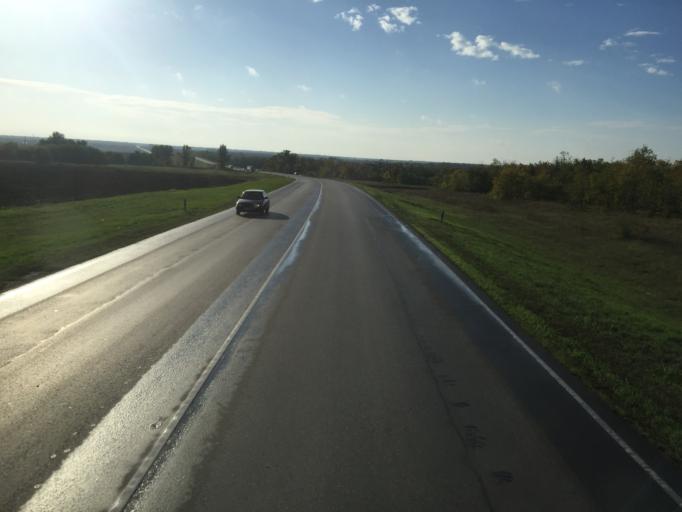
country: RU
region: Rostov
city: Mechetinskaya
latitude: 46.6758
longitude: 40.5269
